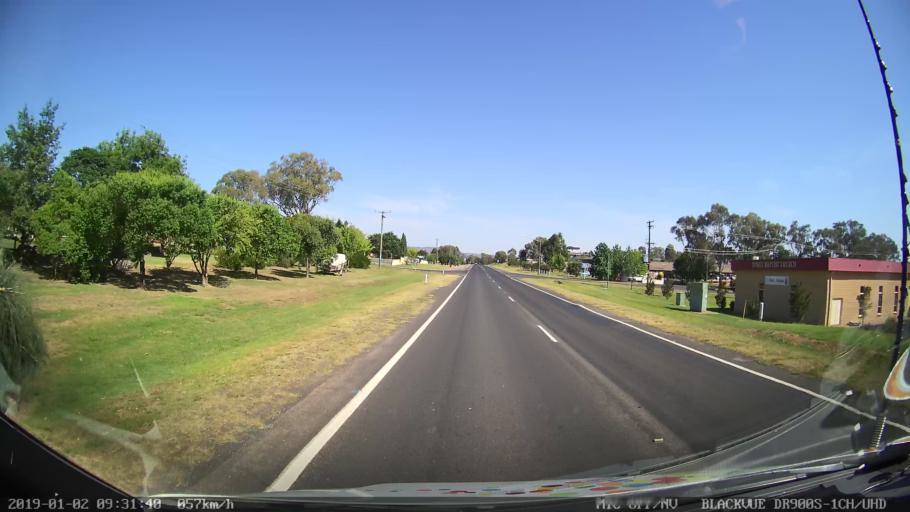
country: AU
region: New South Wales
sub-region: Tumut Shire
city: Tumut
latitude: -35.3171
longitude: 148.2342
